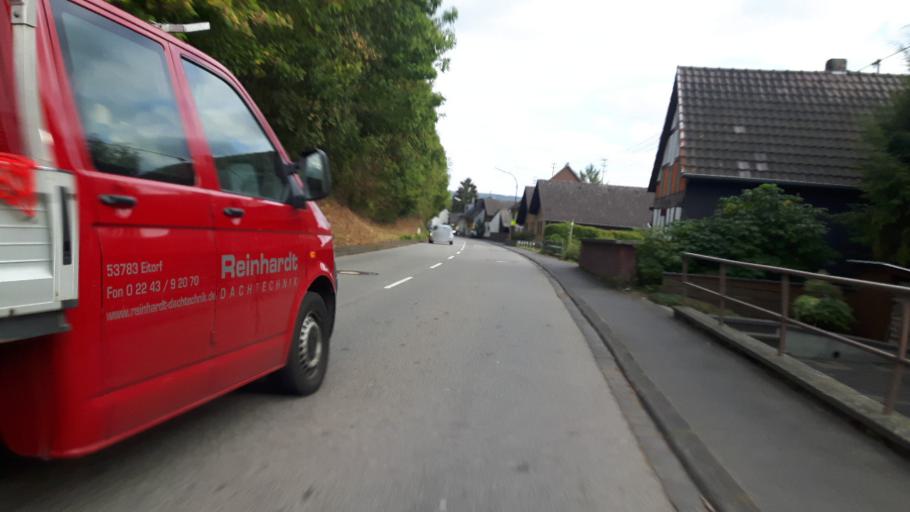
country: DE
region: North Rhine-Westphalia
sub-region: Regierungsbezirk Koln
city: Eitorf
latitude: 50.7714
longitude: 7.4815
